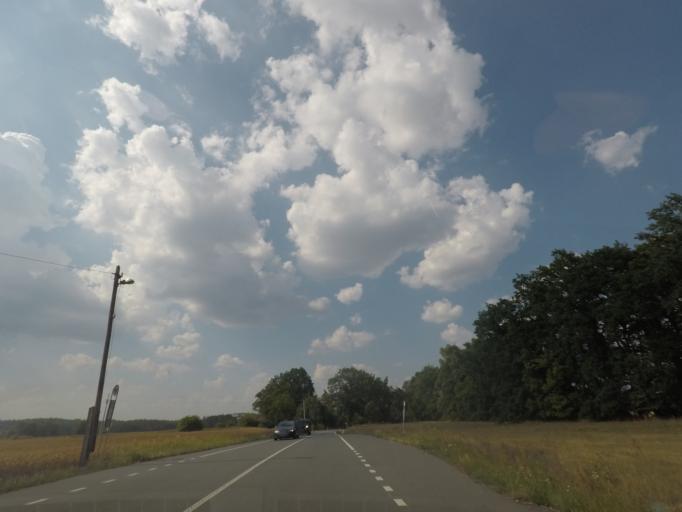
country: CZ
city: Albrechtice nad Orlici
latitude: 50.1333
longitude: 16.0592
